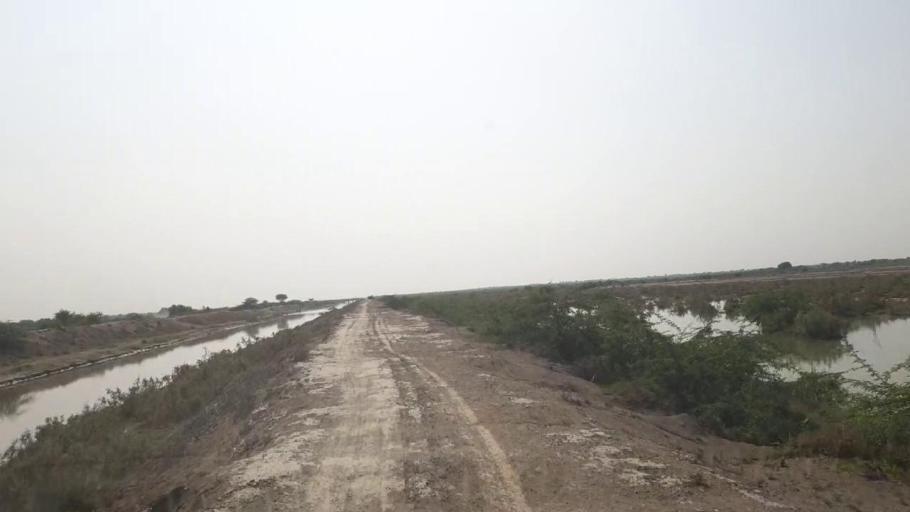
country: PK
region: Sindh
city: Kadhan
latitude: 24.3875
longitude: 68.9008
